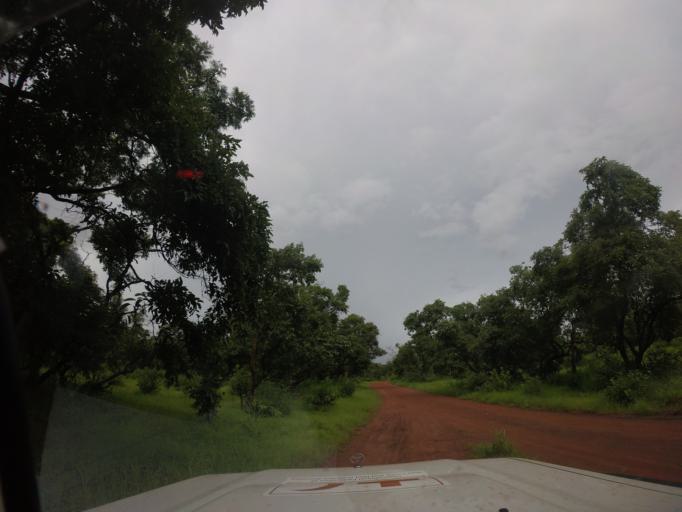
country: SL
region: Northern Province
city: Loma
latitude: 9.8533
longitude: -12.3858
